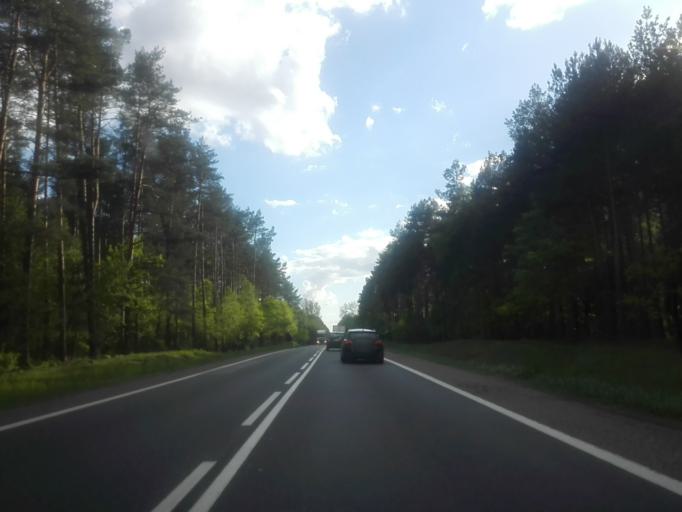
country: PL
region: Masovian Voivodeship
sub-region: Powiat wyszkowski
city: Dlugosiodlo
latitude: 52.7082
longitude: 21.6839
